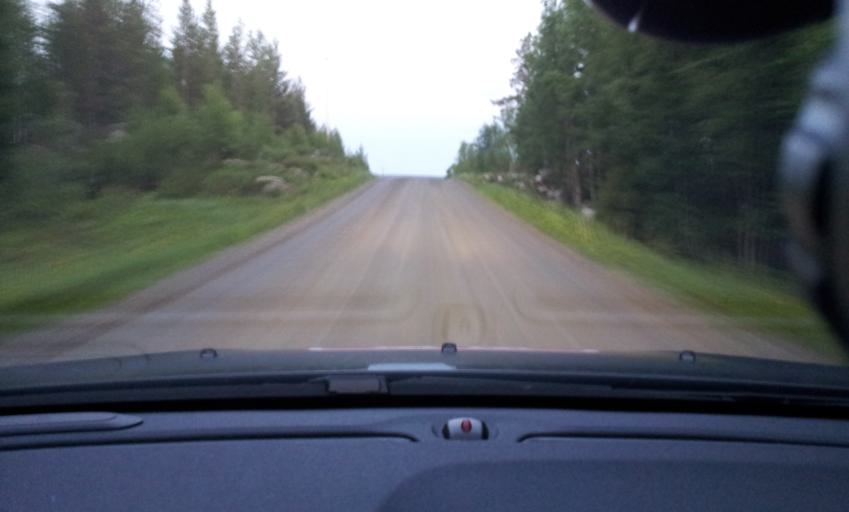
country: SE
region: Vaesternorrland
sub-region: Ange Kommun
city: Fransta
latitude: 62.8082
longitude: 16.0185
